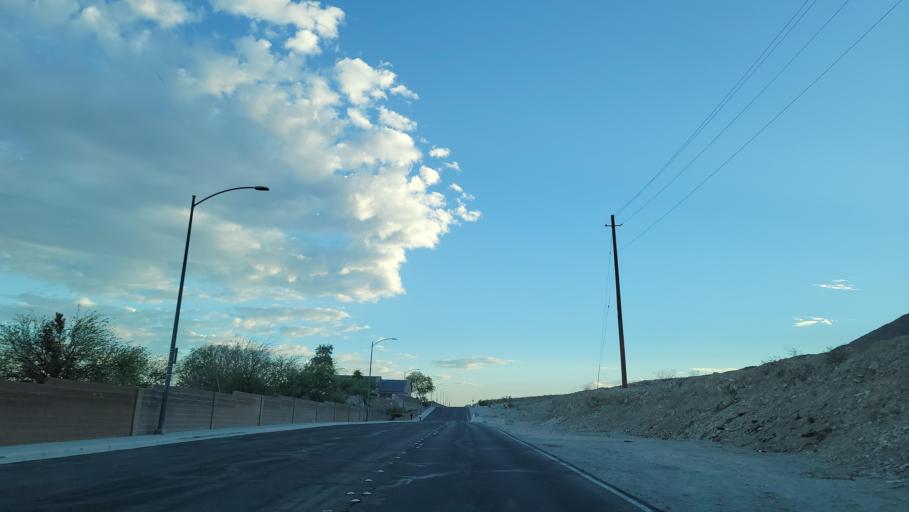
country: US
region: Nevada
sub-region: Clark County
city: Sunrise Manor
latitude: 36.1752
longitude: -115.0167
